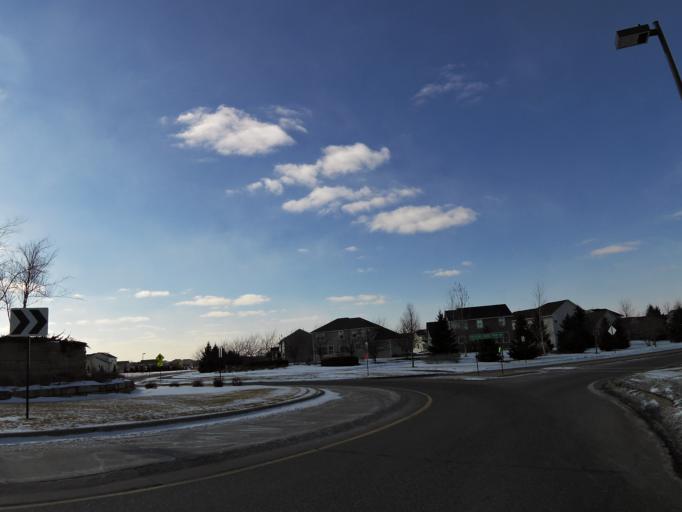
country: US
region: Minnesota
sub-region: Washington County
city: Woodbury
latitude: 44.9021
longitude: -92.8754
